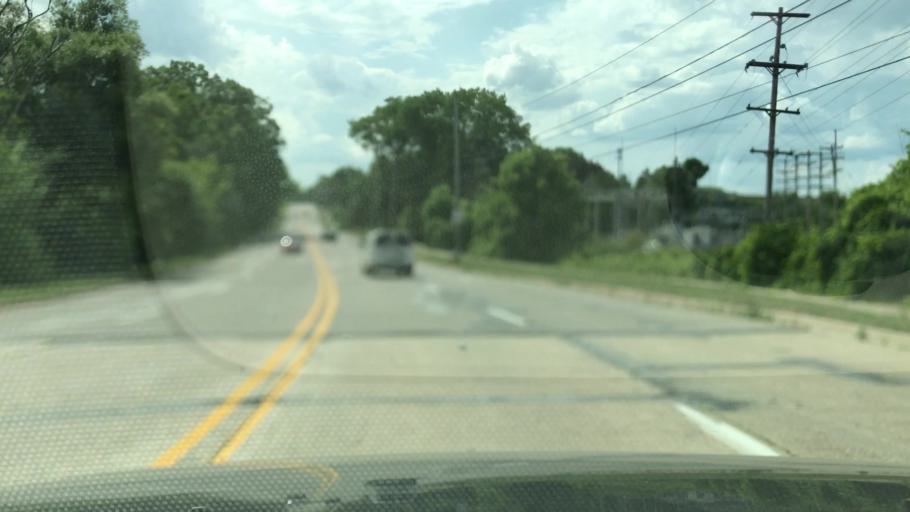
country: US
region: Michigan
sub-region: Kent County
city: East Grand Rapids
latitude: 42.9699
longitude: -85.5936
